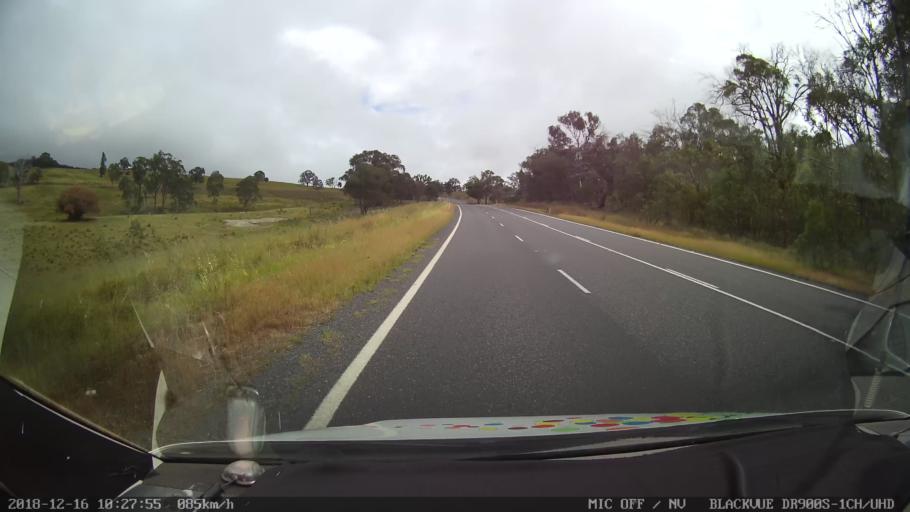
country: AU
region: New South Wales
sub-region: Tenterfield Municipality
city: Carrolls Creek
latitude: -29.1278
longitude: 151.9965
